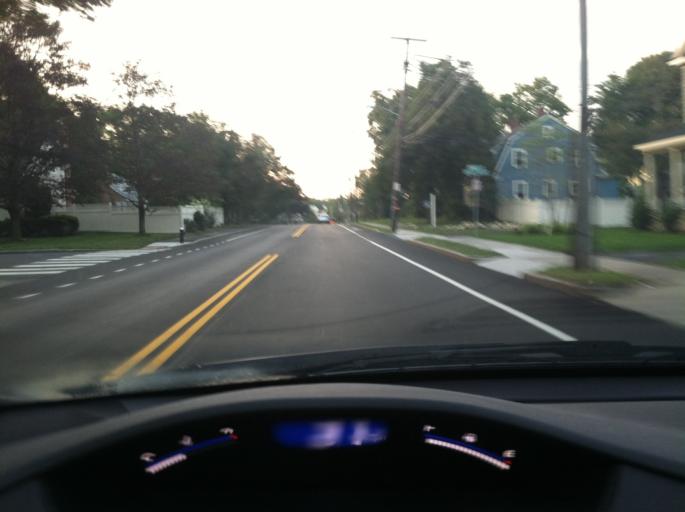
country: US
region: Massachusetts
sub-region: Middlesex County
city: Lexington
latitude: 42.4603
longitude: -71.2387
